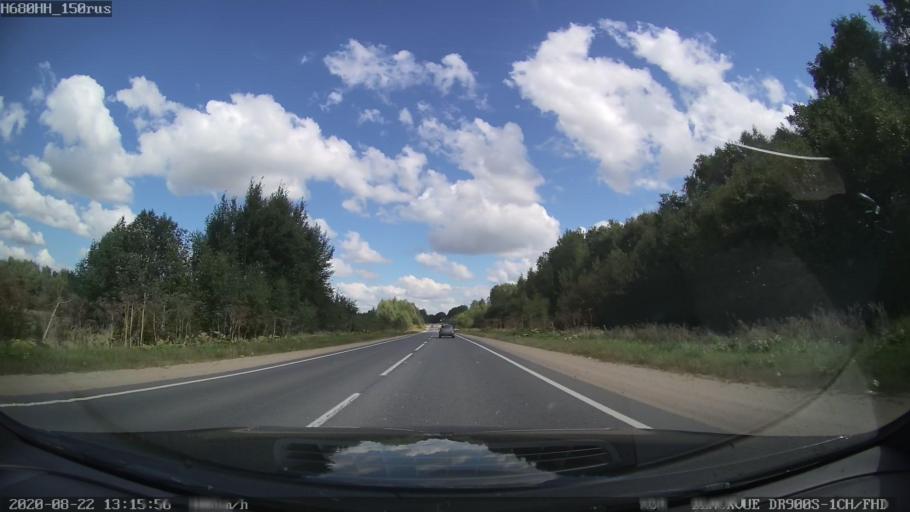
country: RU
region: Tverskaya
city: Bezhetsk
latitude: 57.7604
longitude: 36.6425
